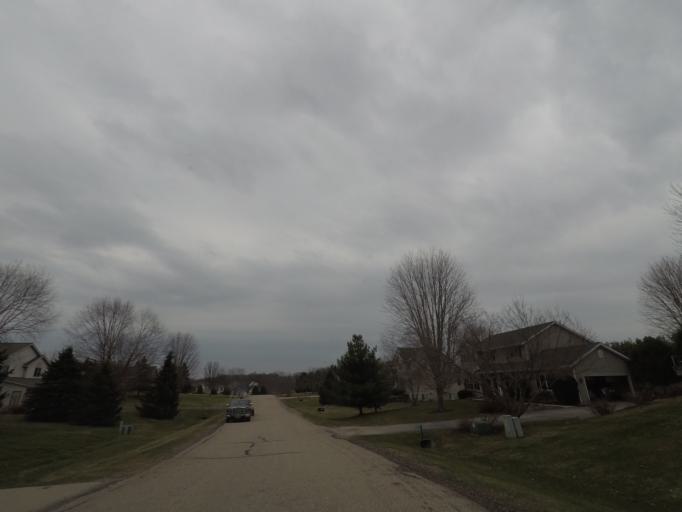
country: US
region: Wisconsin
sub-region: Dane County
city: Middleton
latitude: 43.1176
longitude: -89.5699
